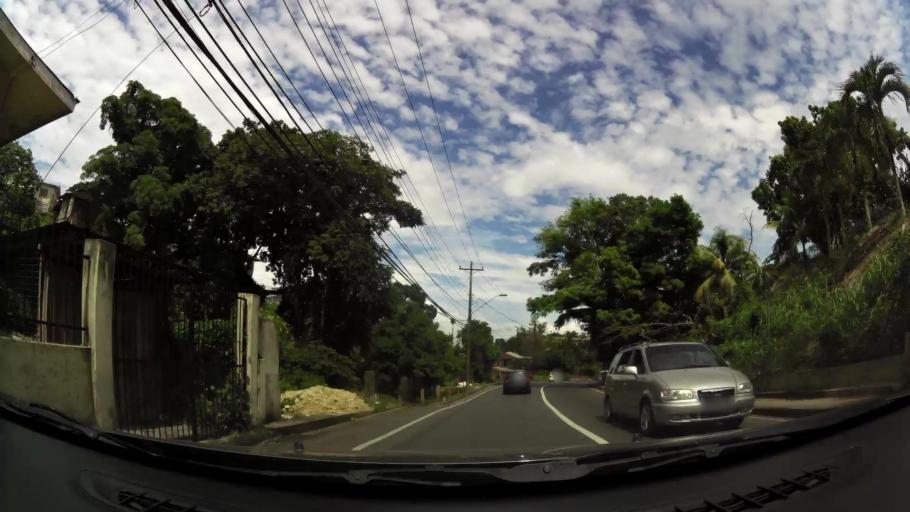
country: TT
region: City of San Fernando
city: San Fernando
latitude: 10.2868
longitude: -61.4567
